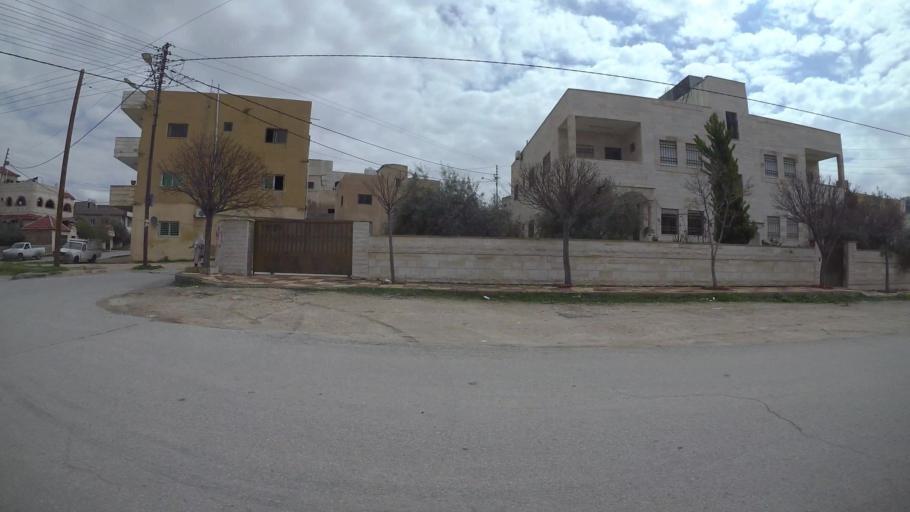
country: JO
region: Amman
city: Al Jubayhah
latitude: 32.0516
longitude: 35.8282
